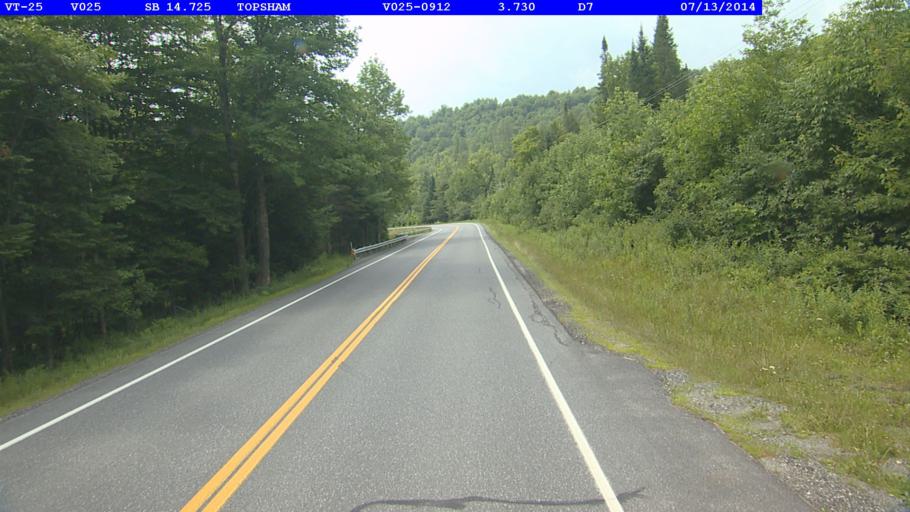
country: US
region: Vermont
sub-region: Orange County
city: Chelsea
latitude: 44.1042
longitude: -72.3190
